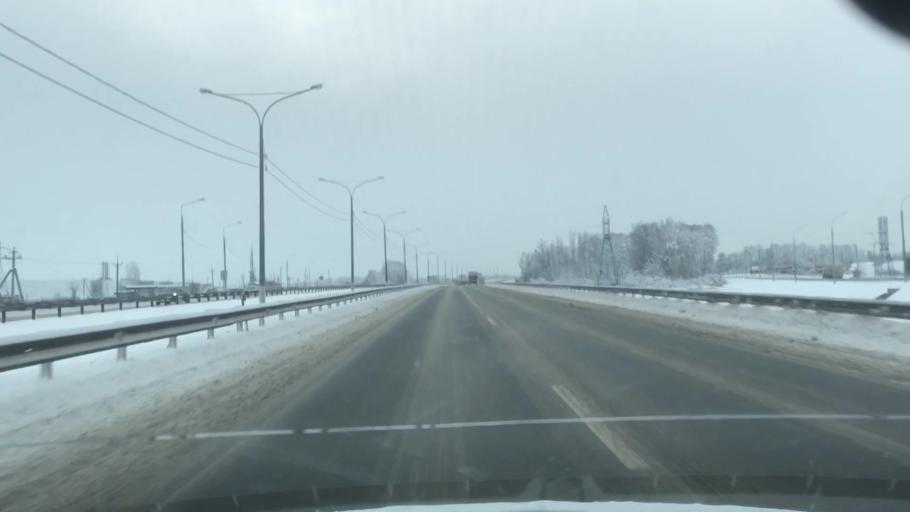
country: RU
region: Moskovskaya
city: Mikhnevo
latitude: 55.1559
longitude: 37.9285
